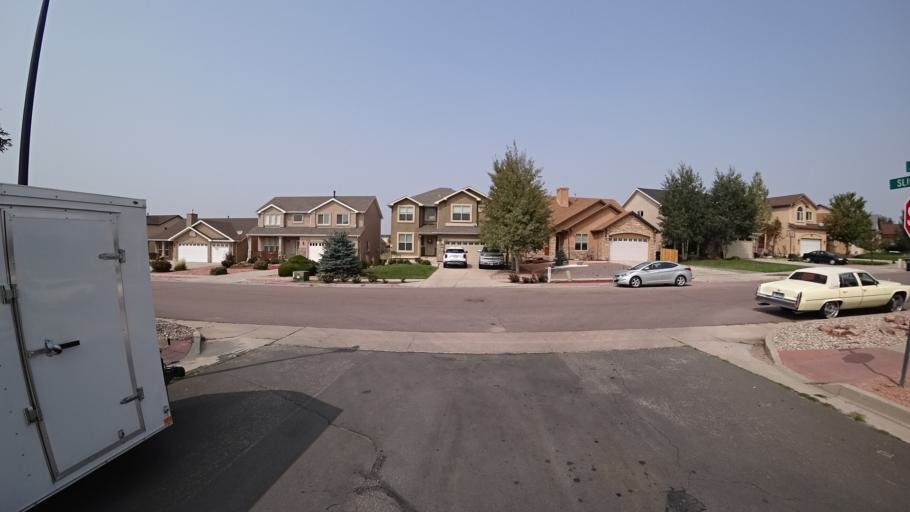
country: US
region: Colorado
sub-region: El Paso County
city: Cimarron Hills
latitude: 38.9239
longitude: -104.7278
